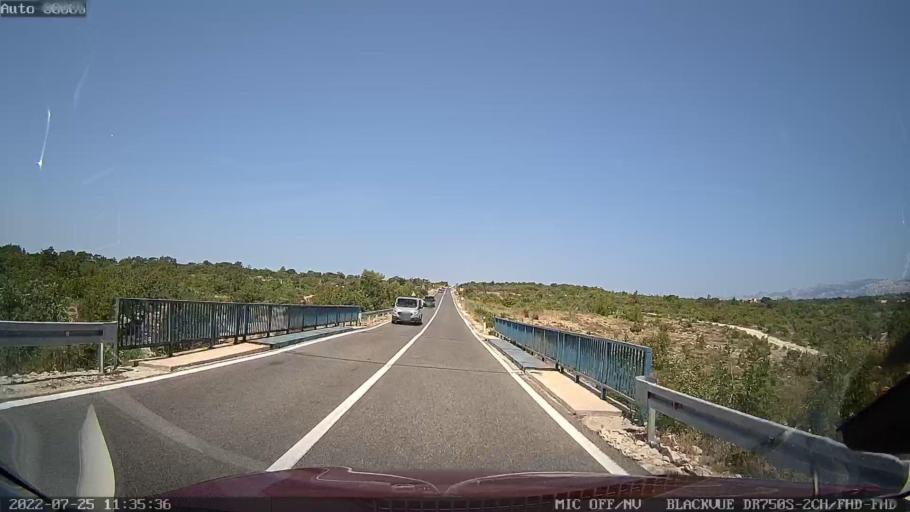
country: HR
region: Zadarska
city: Policnik
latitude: 44.2342
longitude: 15.4059
